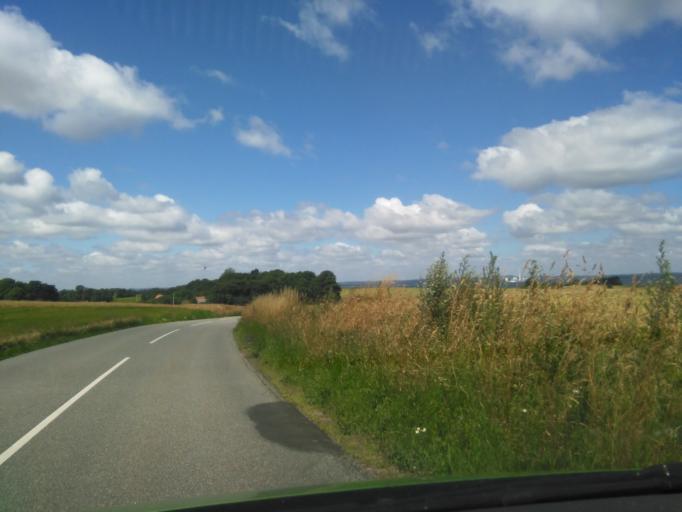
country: DK
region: Central Jutland
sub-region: Syddjurs Kommune
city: Ronde
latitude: 56.1983
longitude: 10.4223
